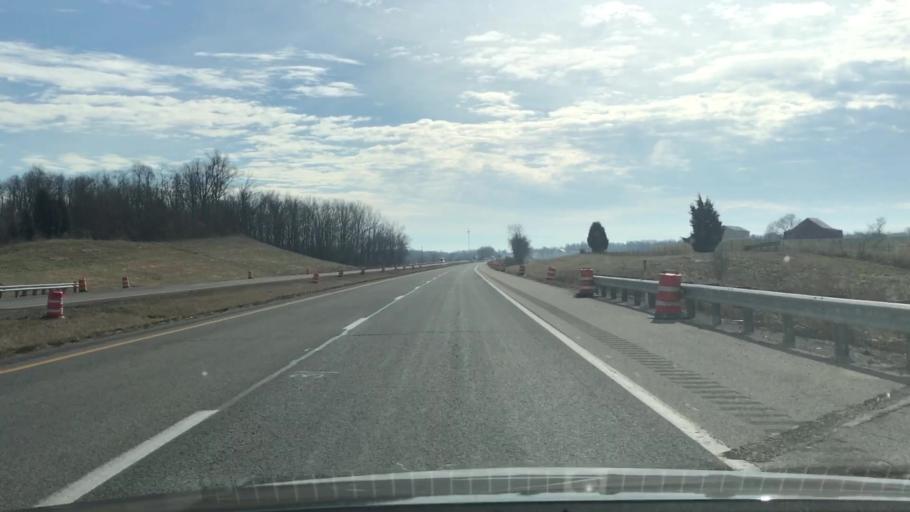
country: US
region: Kentucky
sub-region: Daviess County
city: Masonville
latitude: 37.7172
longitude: -87.0511
